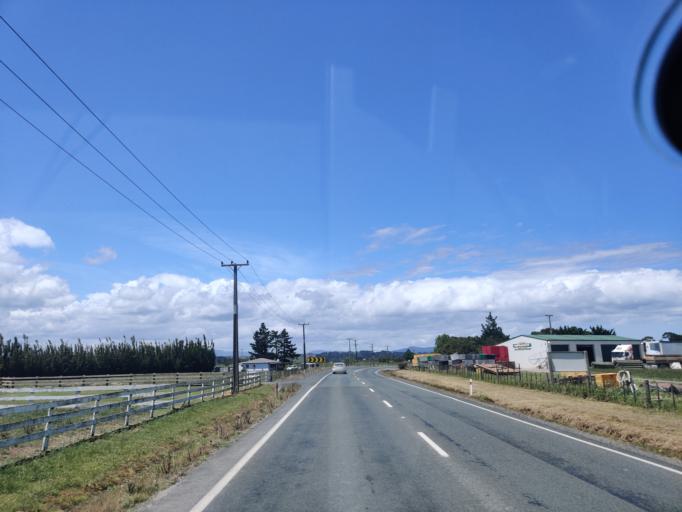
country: NZ
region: Northland
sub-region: Far North District
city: Kaitaia
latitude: -35.0299
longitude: 173.2534
